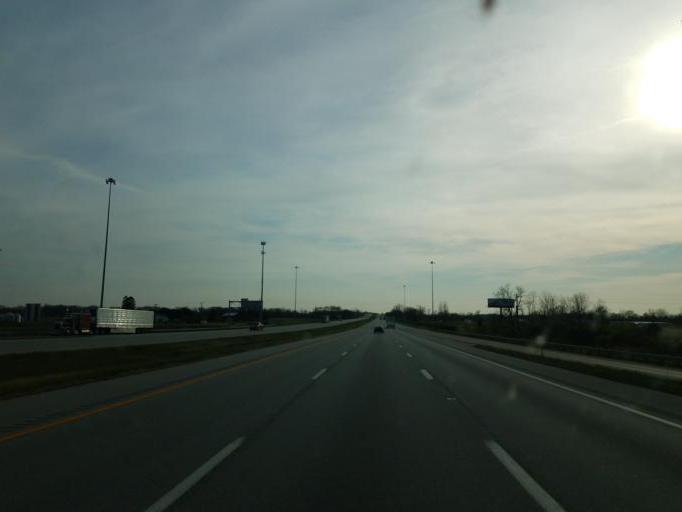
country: US
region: Ohio
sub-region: Fayette County
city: Jeffersonville
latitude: 39.6184
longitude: -83.6100
